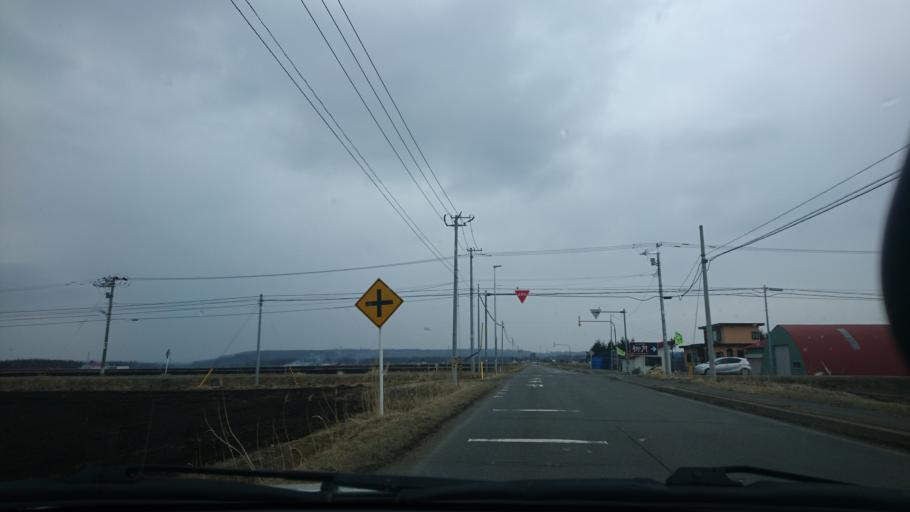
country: JP
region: Hokkaido
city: Otofuke
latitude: 42.9705
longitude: 143.1791
